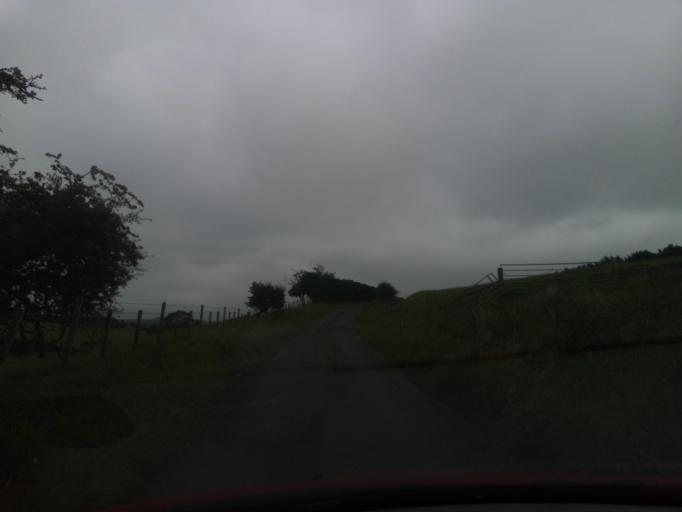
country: GB
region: Scotland
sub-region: Fife
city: Pathhead
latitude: 55.7584
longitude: -2.9341
